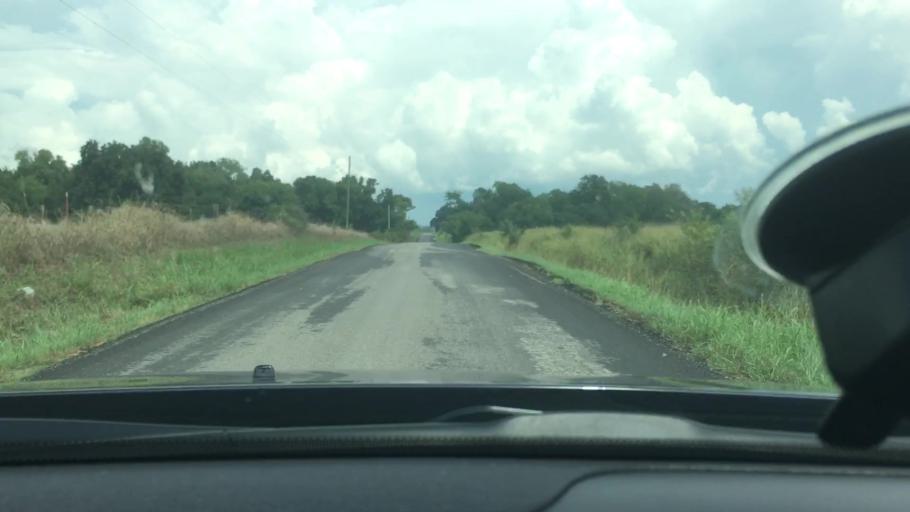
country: US
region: Oklahoma
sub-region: Carter County
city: Dickson
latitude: 34.2122
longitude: -96.8982
